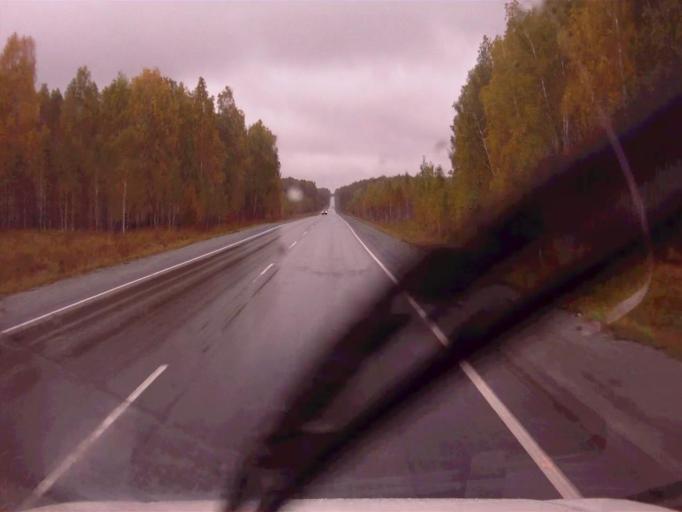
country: RU
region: Chelyabinsk
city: Tayginka
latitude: 55.5133
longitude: 60.6394
